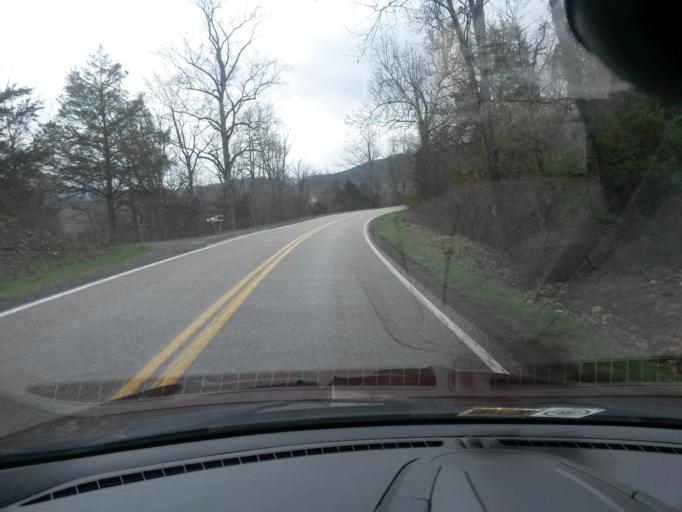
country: US
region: Virginia
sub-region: Alleghany County
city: Clifton Forge
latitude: 37.8946
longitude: -79.7504
